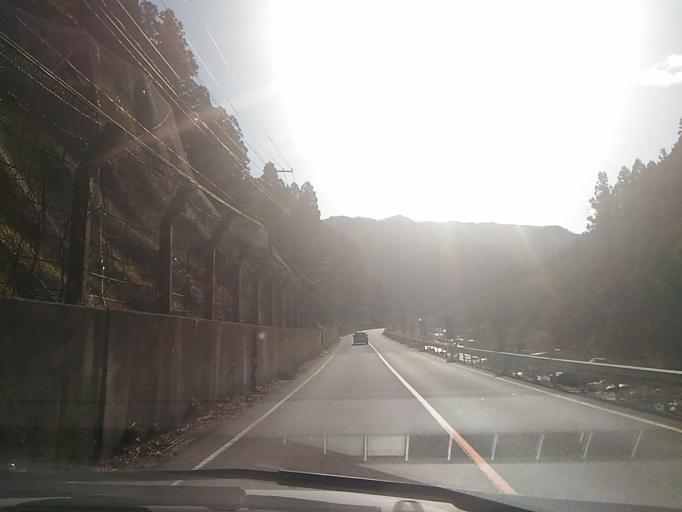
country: JP
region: Fukushima
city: Ishikawa
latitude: 37.0434
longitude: 140.6187
